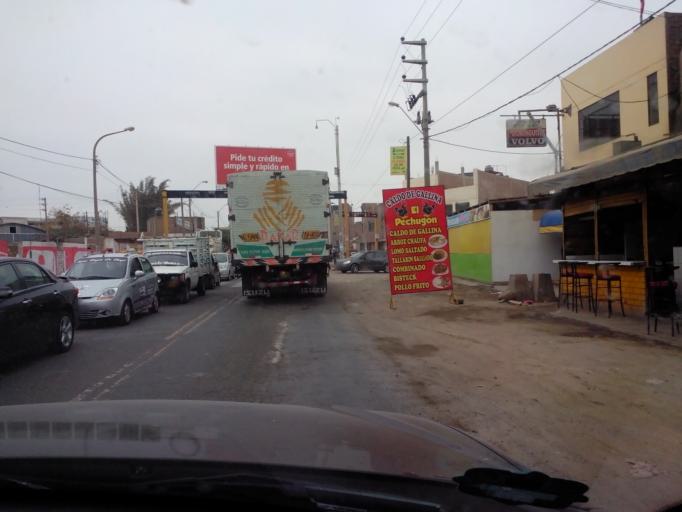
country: PE
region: Ica
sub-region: Provincia de Chincha
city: Chincha Alta
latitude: -13.4186
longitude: -76.1383
